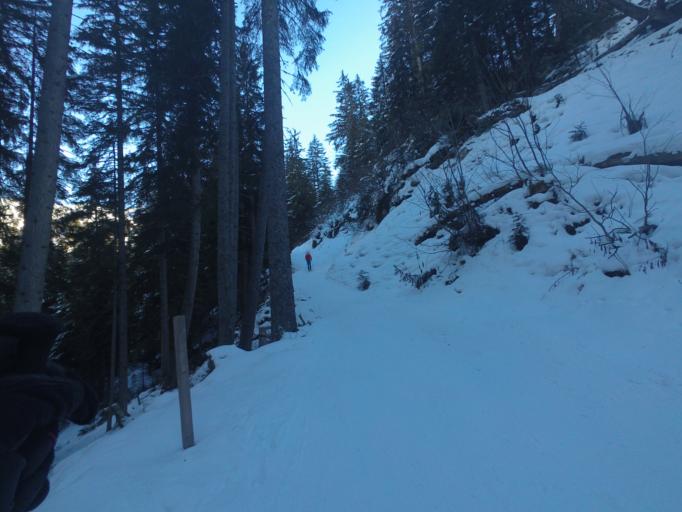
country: AT
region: Salzburg
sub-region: Politischer Bezirk Sankt Johann im Pongau
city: Huttschlag
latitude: 47.1808
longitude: 13.2770
